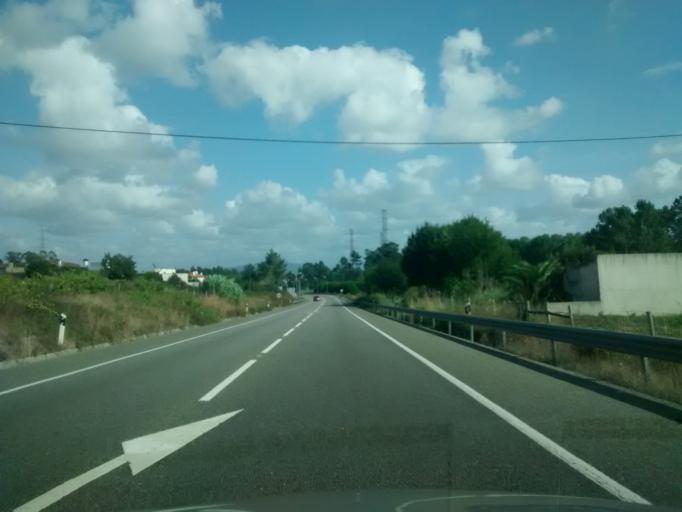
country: PT
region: Aveiro
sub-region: Anadia
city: Sangalhos
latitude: 40.4709
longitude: -8.4692
